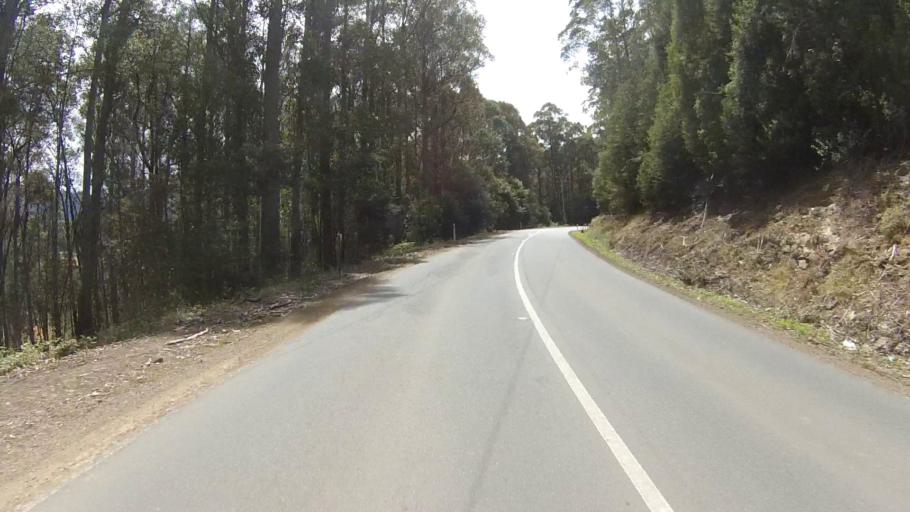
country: AU
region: Tasmania
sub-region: Kingborough
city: Kettering
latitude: -43.1276
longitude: 147.1677
